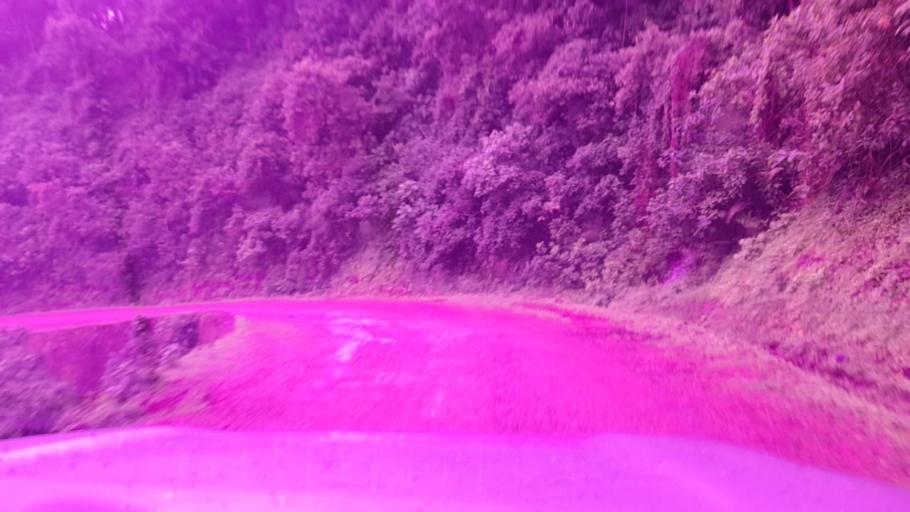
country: ET
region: Southern Nations, Nationalities, and People's Region
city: Bonga
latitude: 7.5078
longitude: 36.0638
